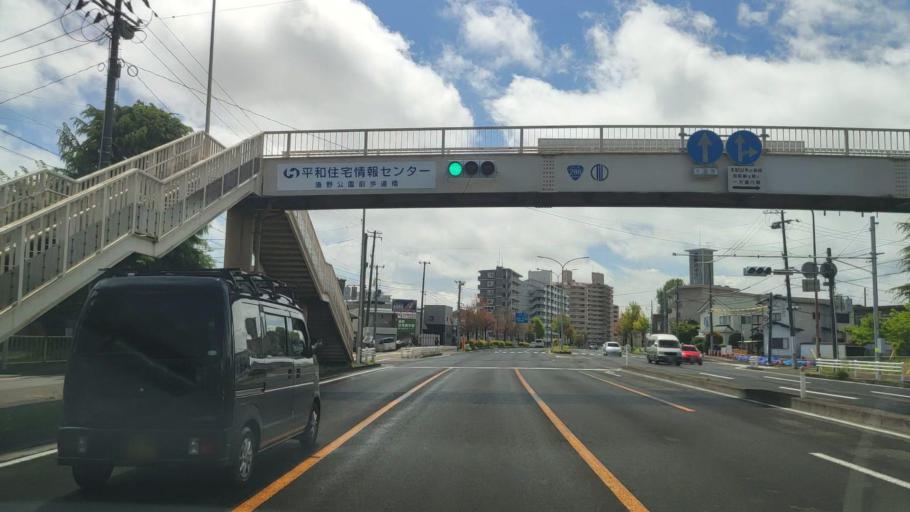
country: JP
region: Miyagi
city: Sendai
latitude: 38.2320
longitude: 140.8773
